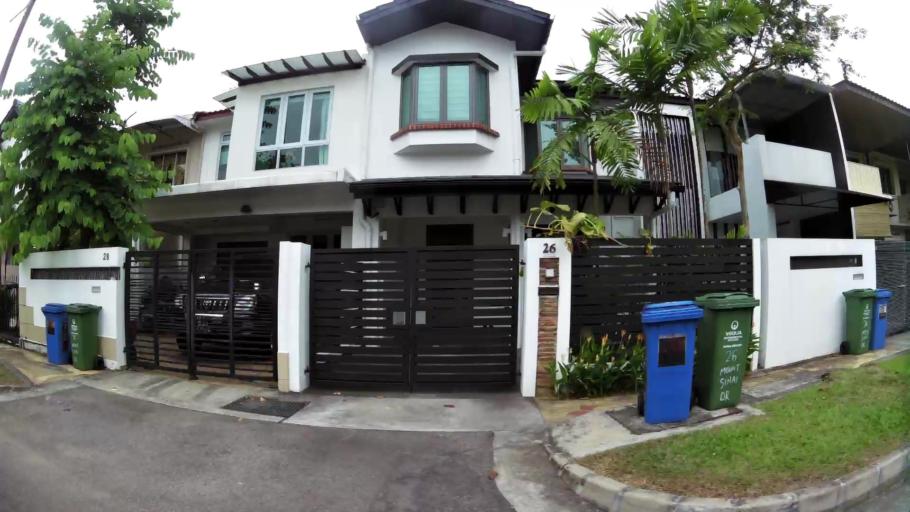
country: SG
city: Singapore
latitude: 1.3164
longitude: 103.7818
